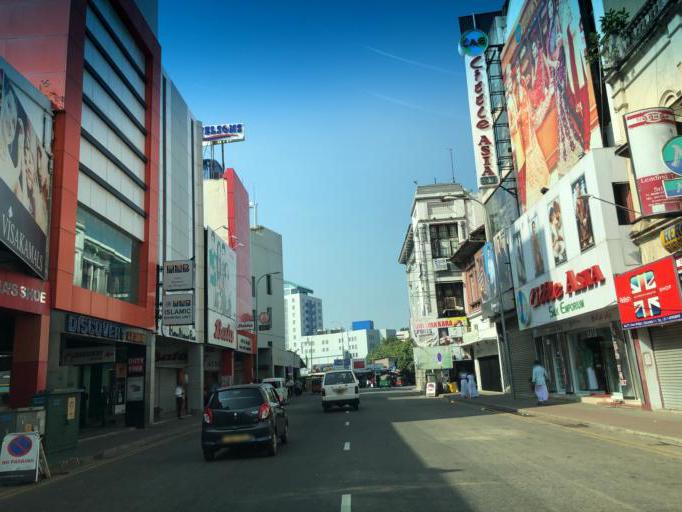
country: LK
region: Western
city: Colombo
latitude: 6.9372
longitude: 79.8504
